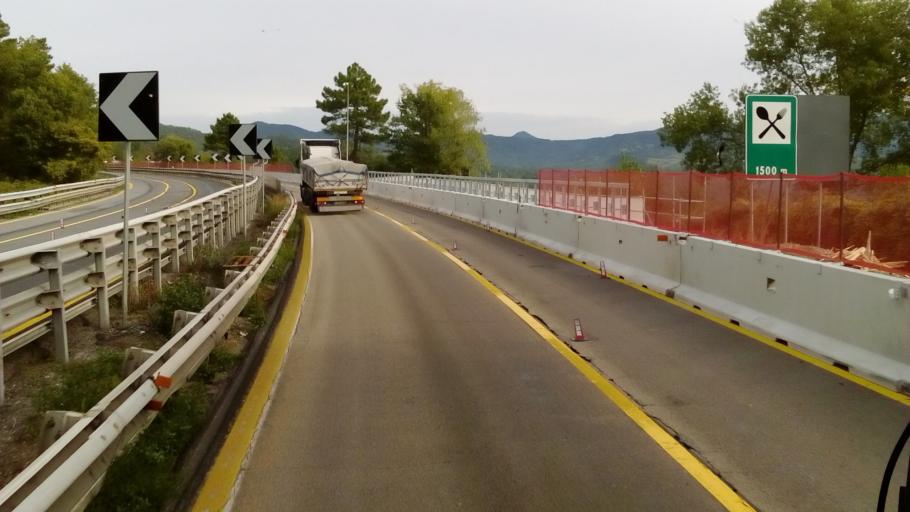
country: IT
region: Tuscany
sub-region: Province of Florence
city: Barberino di Mugello
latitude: 44.0176
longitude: 11.2244
